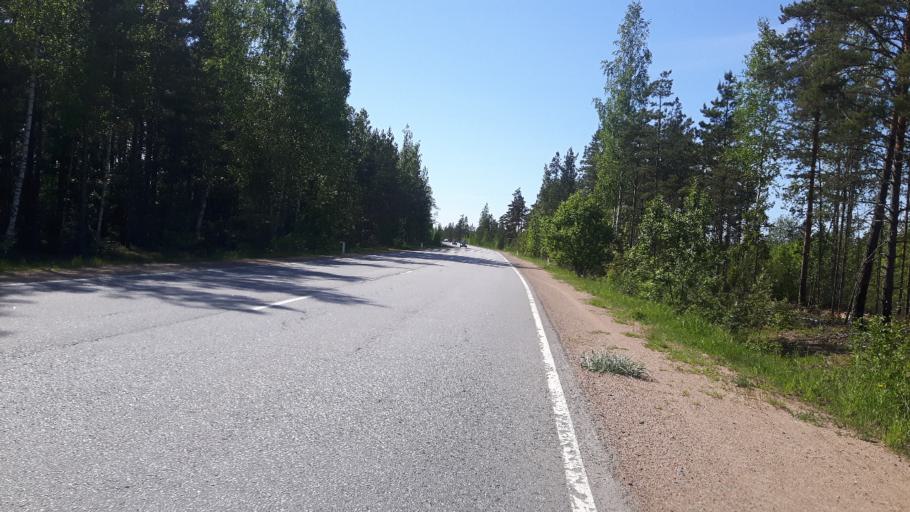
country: RU
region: Leningrad
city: Sista-Palkino
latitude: 59.7692
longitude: 28.7911
